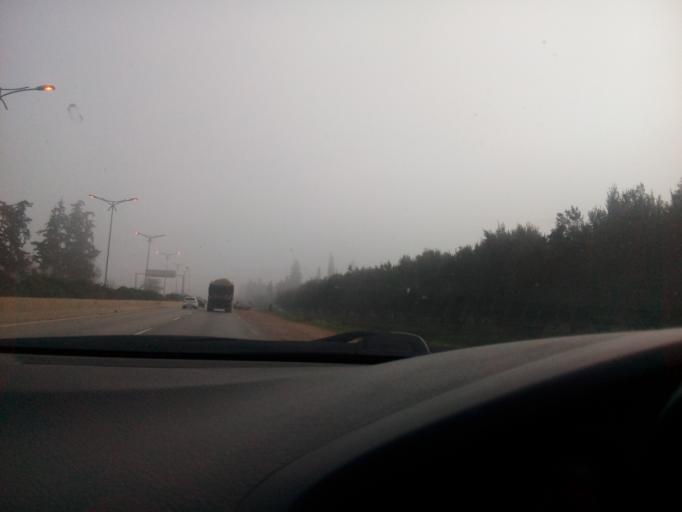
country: DZ
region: Oran
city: Bou Tlelis
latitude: 35.5888
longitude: -0.8041
